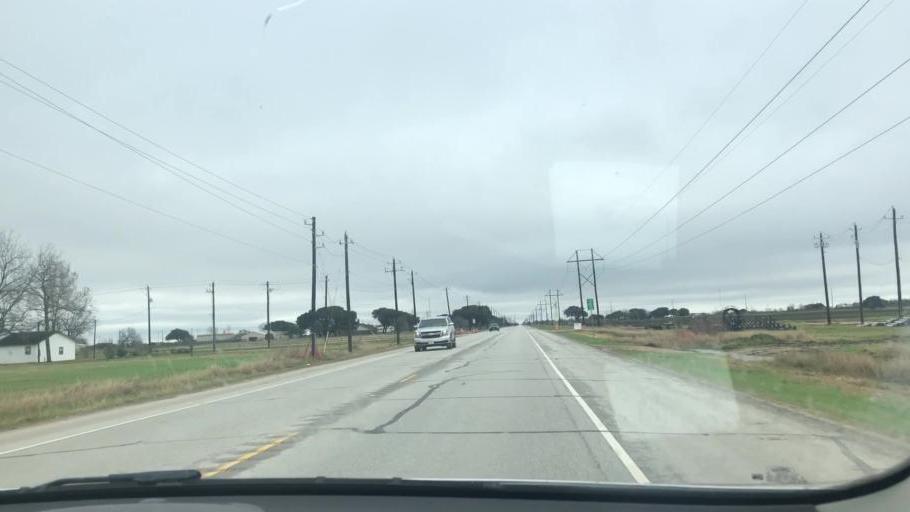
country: US
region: Texas
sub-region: Wharton County
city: Boling
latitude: 29.2063
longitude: -96.0239
